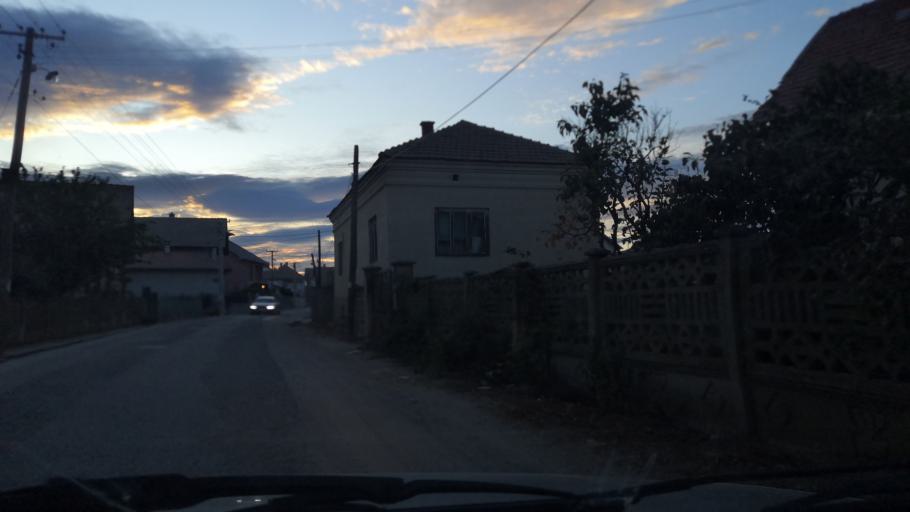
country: RO
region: Mehedinti
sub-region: Comuna Gogosu
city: Balta Verde
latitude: 44.2934
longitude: 22.5906
